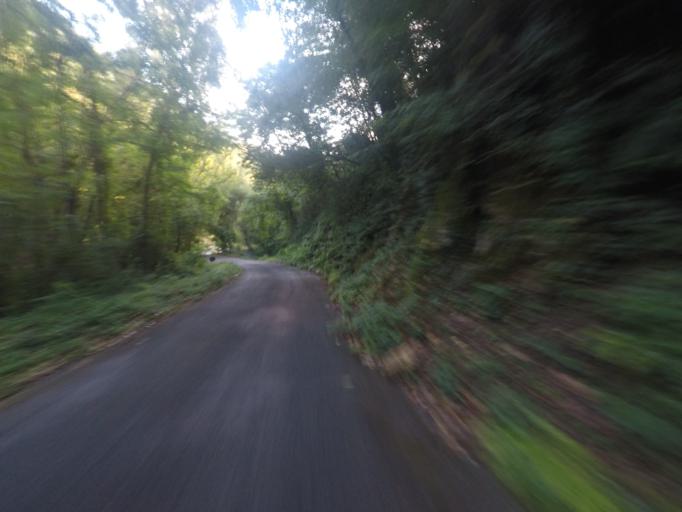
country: IT
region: Tuscany
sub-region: Provincia di Lucca
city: Pescaglia
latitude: 43.9424
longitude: 10.3935
